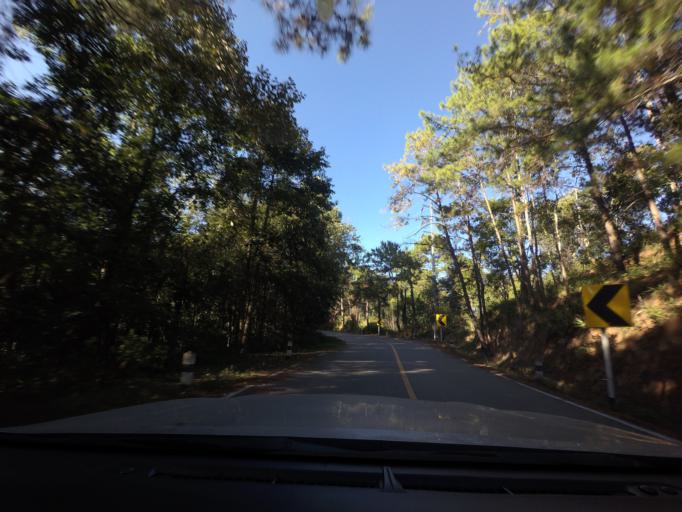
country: TH
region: Mae Hong Son
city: Mae Hi
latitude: 19.2756
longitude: 98.6229
